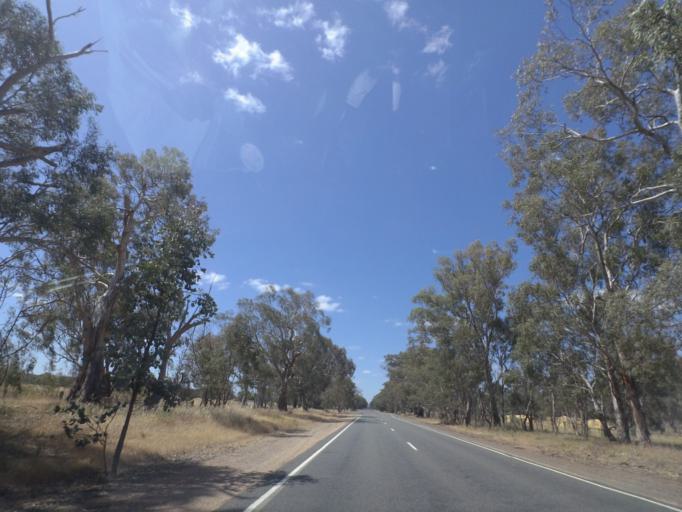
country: AU
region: Victoria
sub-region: Wangaratta
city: Wangaratta
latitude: -36.4312
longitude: 146.2533
